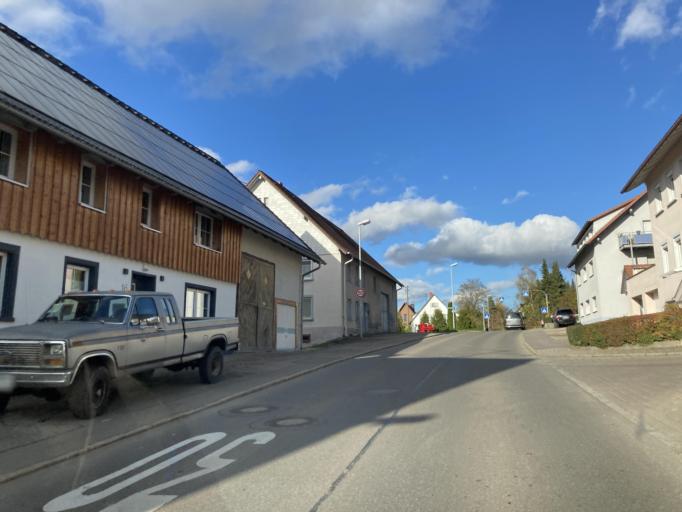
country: DE
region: Baden-Wuerttemberg
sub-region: Freiburg Region
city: Donaueschingen
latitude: 48.0075
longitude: 8.4685
